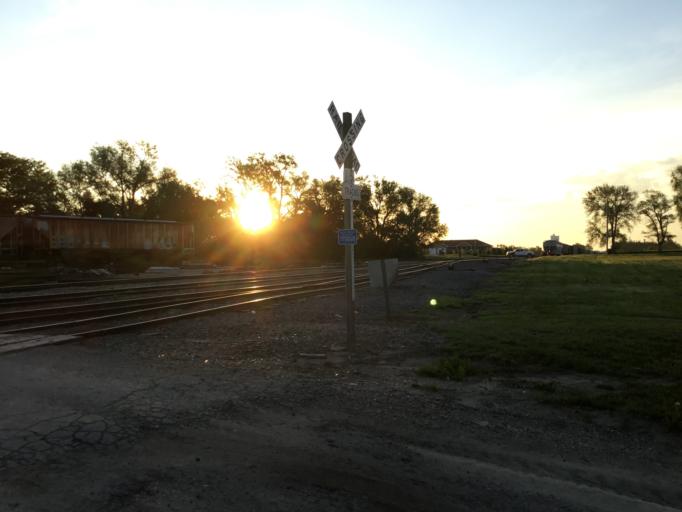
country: US
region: Kansas
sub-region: Mitchell County
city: Beloit
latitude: 39.4554
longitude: -98.1038
